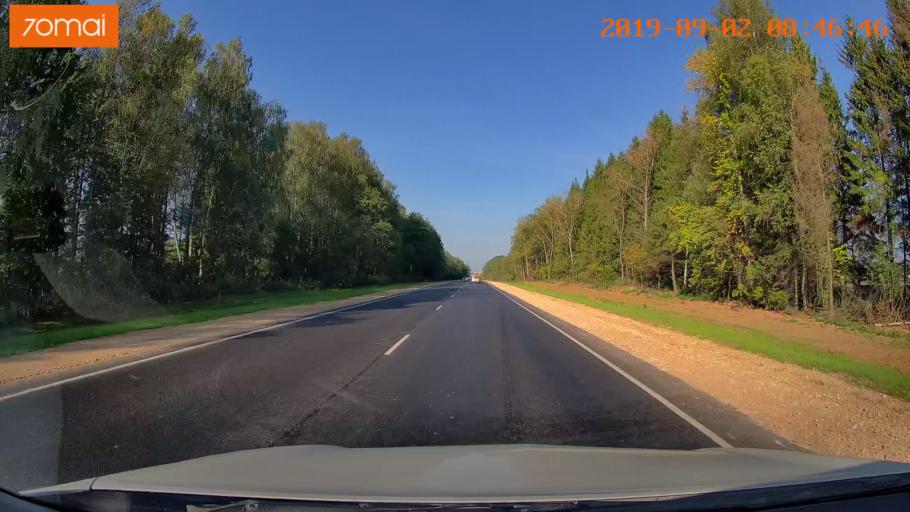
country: RU
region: Kaluga
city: Medyn'
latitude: 54.9684
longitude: 35.9703
